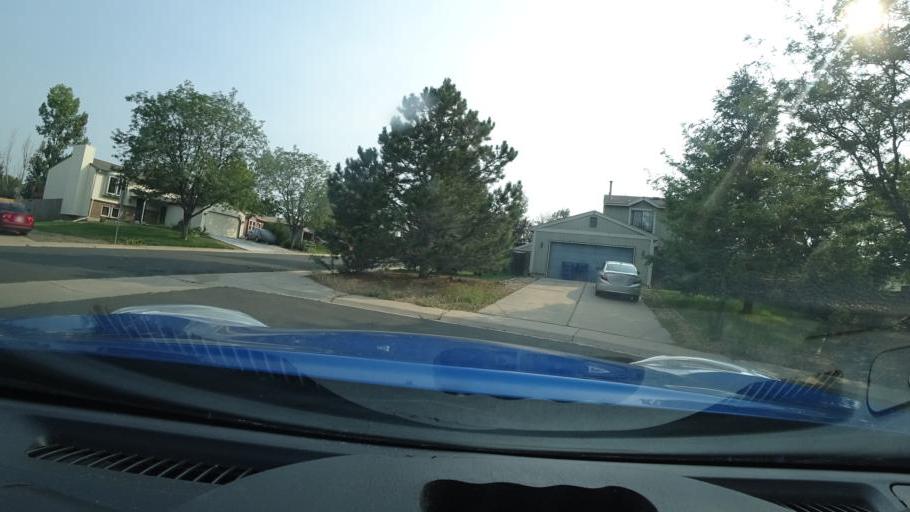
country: US
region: Colorado
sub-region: Adams County
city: Aurora
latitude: 39.6659
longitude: -104.7816
